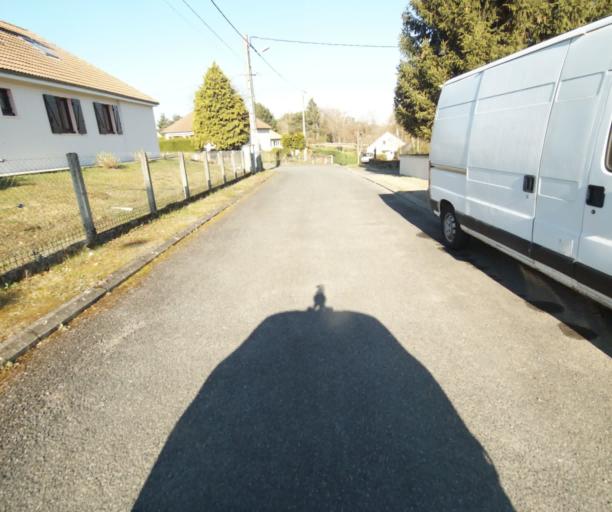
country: FR
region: Limousin
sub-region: Departement de la Correze
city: Correze
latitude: 45.3278
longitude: 1.8803
